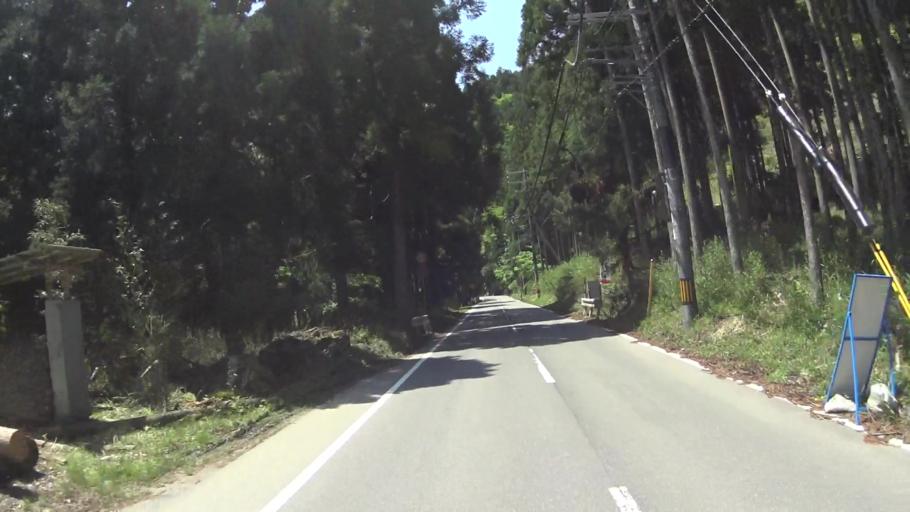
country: JP
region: Kyoto
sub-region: Kyoto-shi
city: Kamigyo-ku
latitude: 35.1962
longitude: 135.7077
